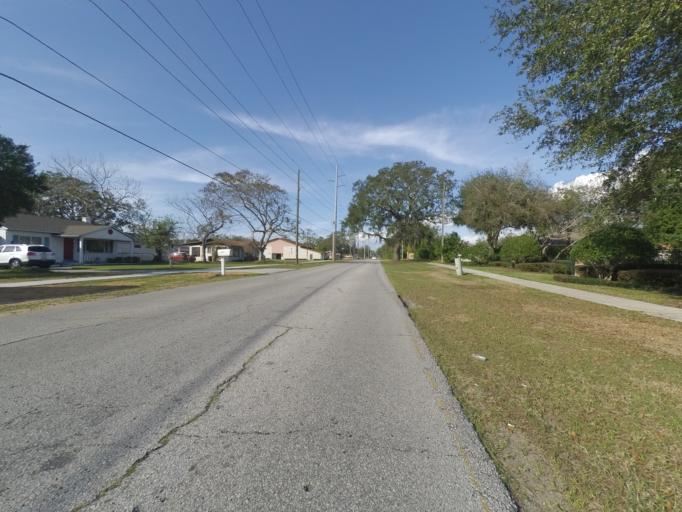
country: US
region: Florida
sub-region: Lake County
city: Eustis
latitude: 28.8335
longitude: -81.6835
